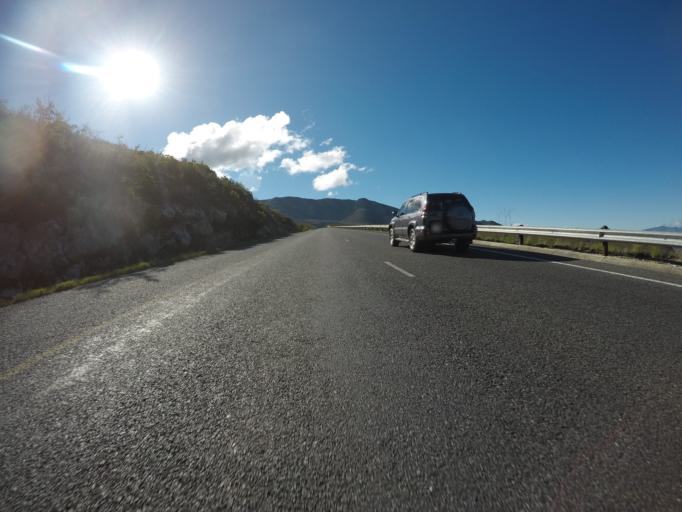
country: ZA
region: Western Cape
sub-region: Overberg District Municipality
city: Grabouw
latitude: -34.2224
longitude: 19.1721
